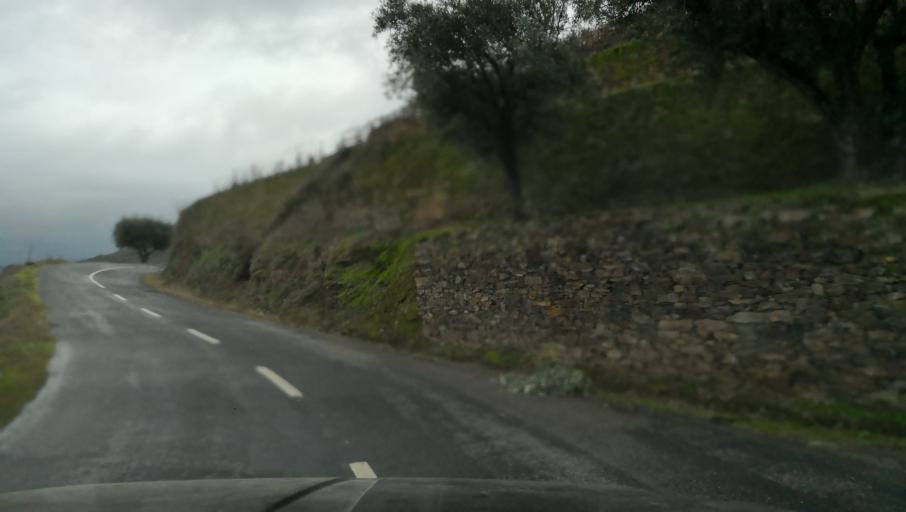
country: PT
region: Vila Real
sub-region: Santa Marta de Penaguiao
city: Santa Marta de Penaguiao
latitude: 41.2265
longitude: -7.7410
